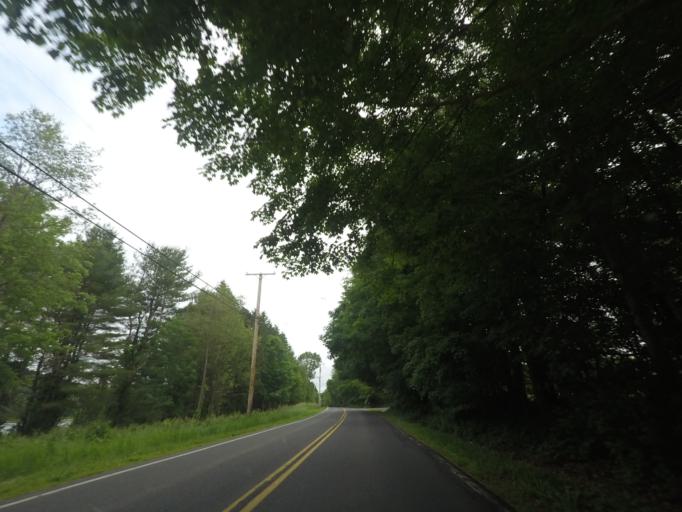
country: US
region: New York
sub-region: Dutchess County
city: Pine Plains
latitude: 41.9745
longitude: -73.5056
